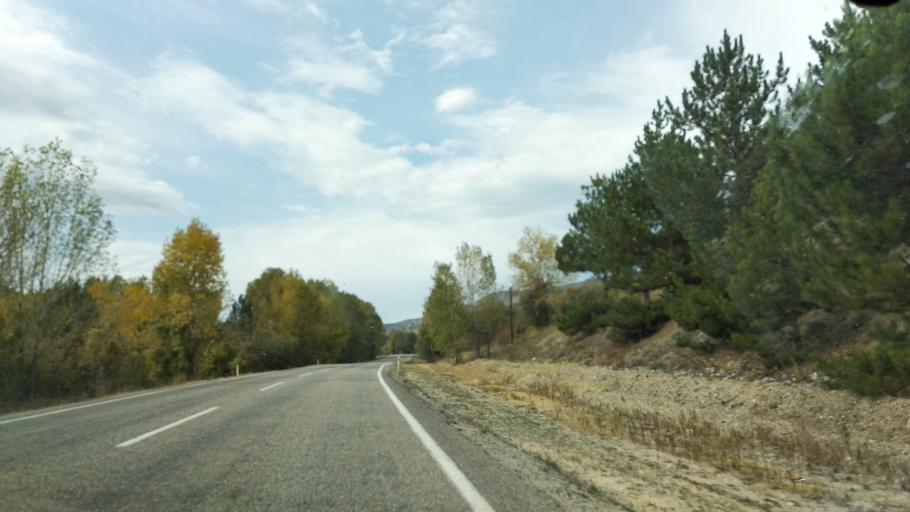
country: TR
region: Ankara
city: Nallihan
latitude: 40.3079
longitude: 31.2782
